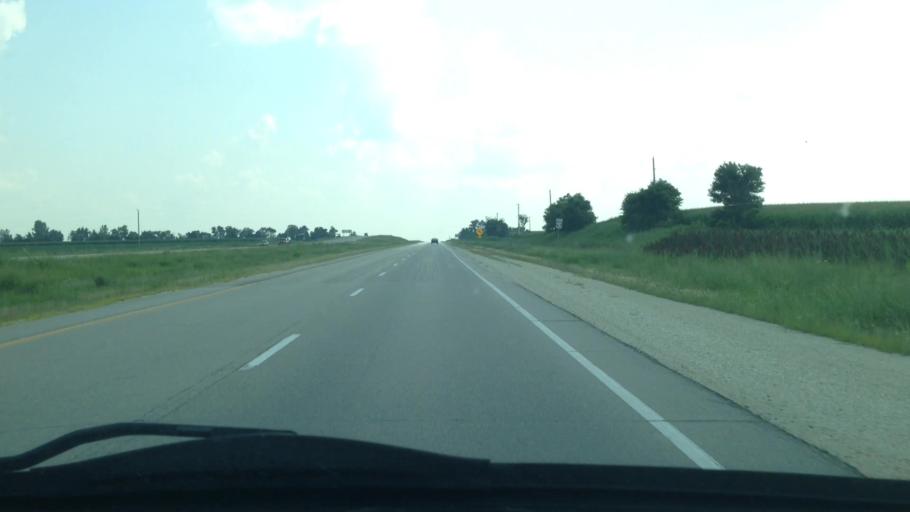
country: US
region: Iowa
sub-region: Bremer County
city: Denver
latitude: 42.7067
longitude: -92.3376
